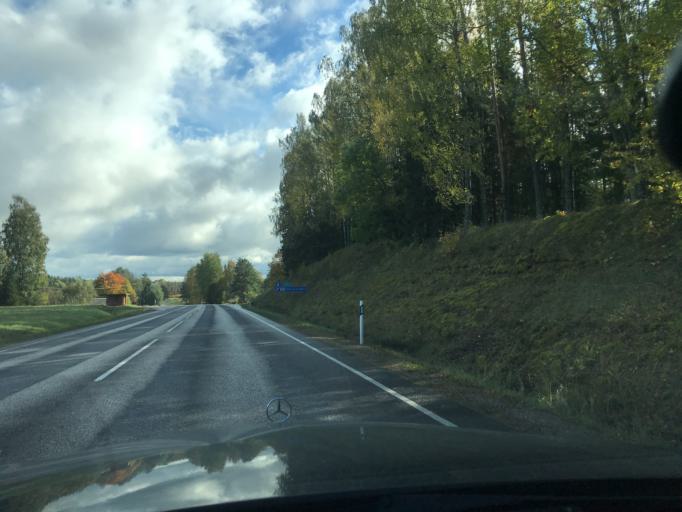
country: EE
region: Vorumaa
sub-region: Voru linn
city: Voru
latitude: 57.7706
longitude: 27.1524
